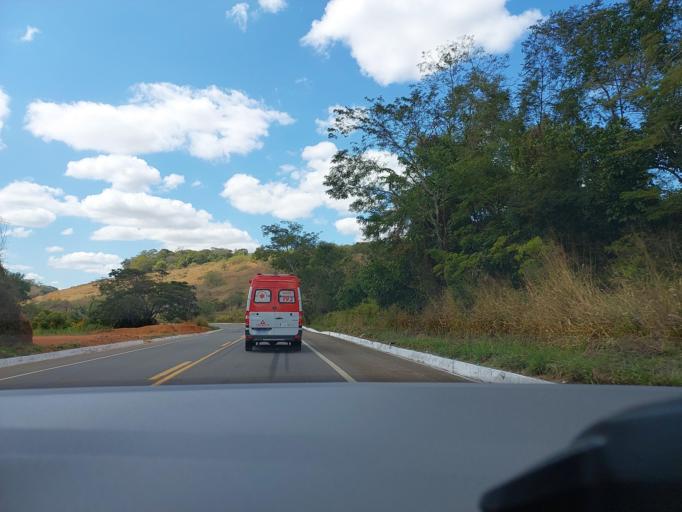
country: BR
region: Minas Gerais
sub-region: Muriae
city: Muriae
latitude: -21.1360
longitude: -42.2979
